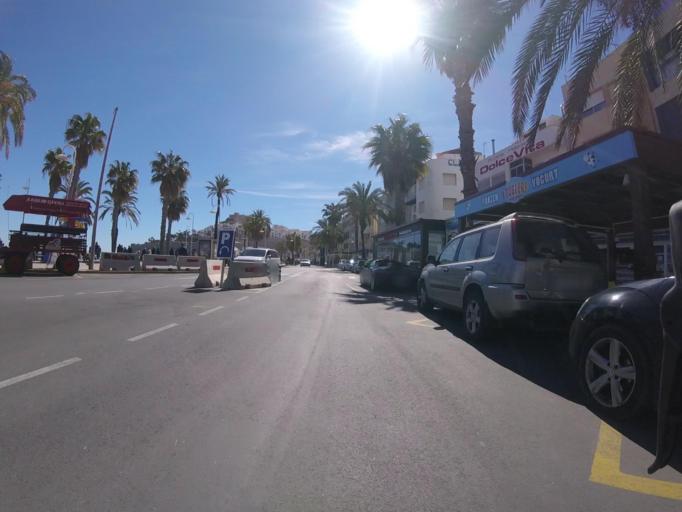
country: ES
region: Valencia
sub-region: Provincia de Castello
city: Peniscola
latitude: 40.3601
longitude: 0.4032
